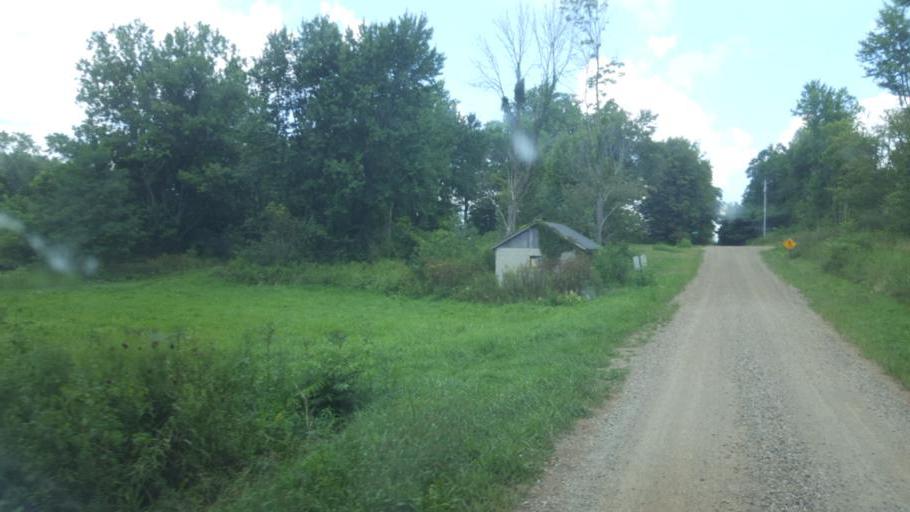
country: US
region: Ohio
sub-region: Knox County
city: Centerburg
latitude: 40.3870
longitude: -82.6314
